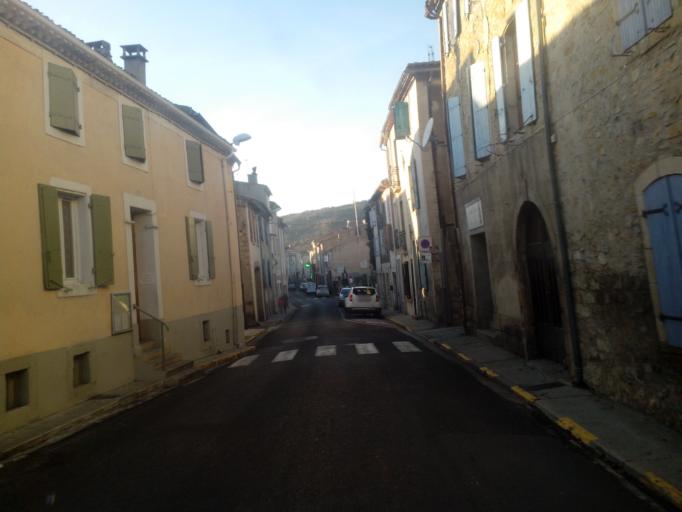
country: FR
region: Languedoc-Roussillon
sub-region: Departement de l'Aude
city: Esperaza
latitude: 42.9346
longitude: 2.2235
